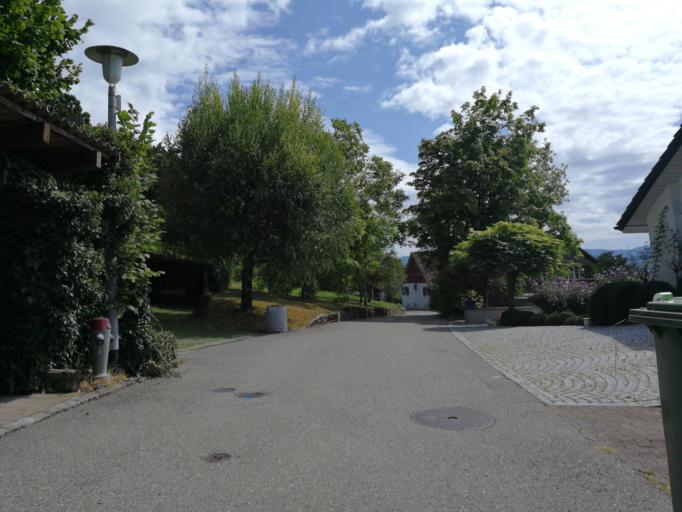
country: CH
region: Zurich
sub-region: Bezirk Meilen
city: Herrliberg
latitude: 47.2836
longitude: 8.6154
